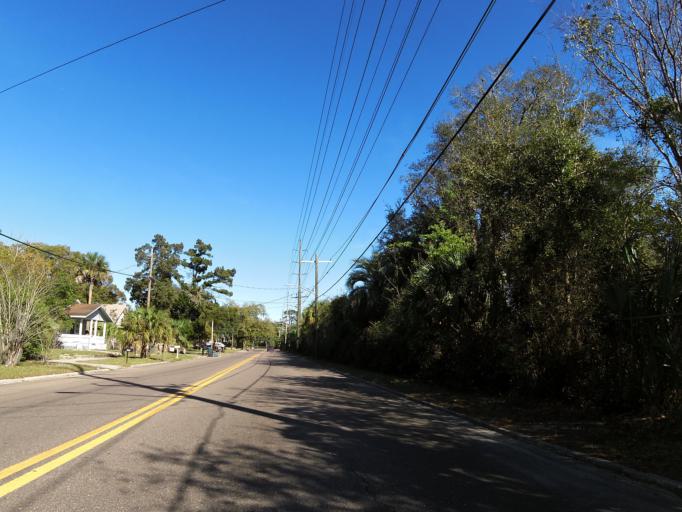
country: US
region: Florida
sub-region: Duval County
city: Jacksonville
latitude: 30.3727
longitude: -81.6429
